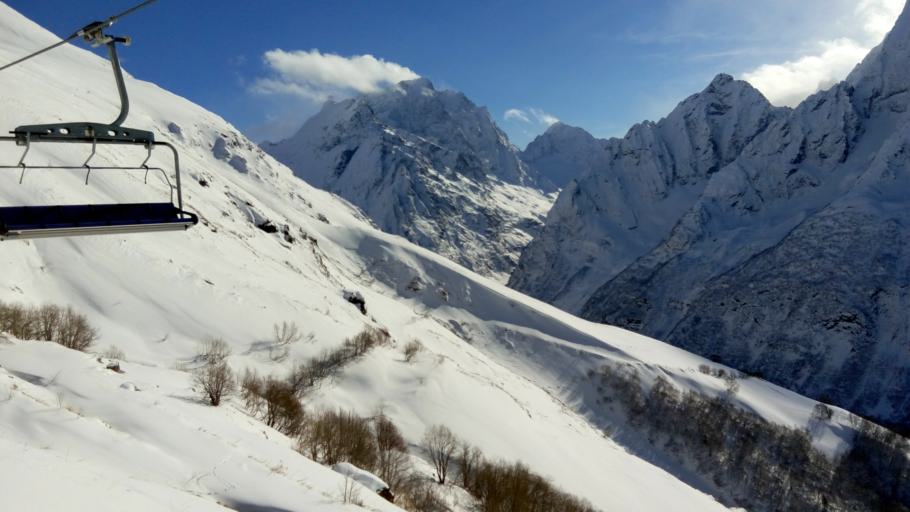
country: RU
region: Karachayevo-Cherkesiya
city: Teberda
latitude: 43.2913
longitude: 41.6537
